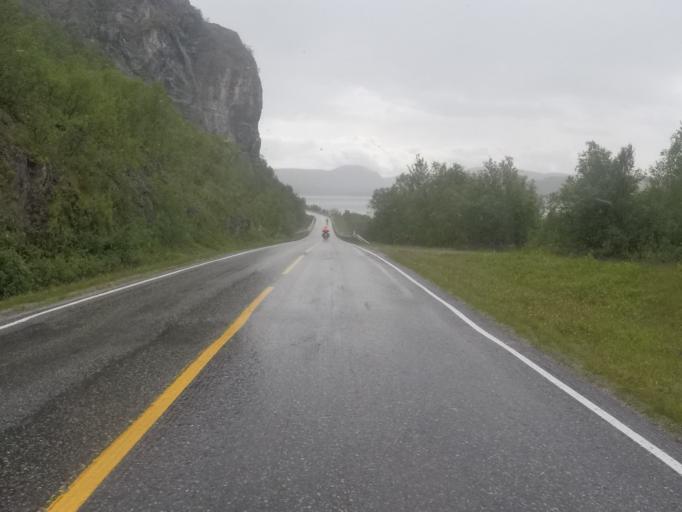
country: NO
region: Finnmark Fylke
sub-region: Porsanger
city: Lakselv
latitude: 69.8579
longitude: 25.0499
